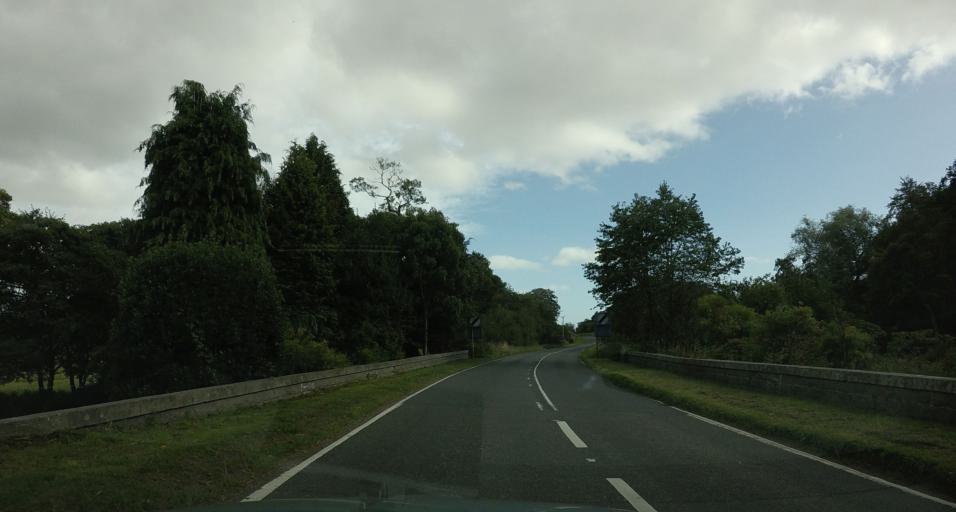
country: GB
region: Scotland
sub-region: Aberdeenshire
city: Kemnay
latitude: 57.1717
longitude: -2.4070
